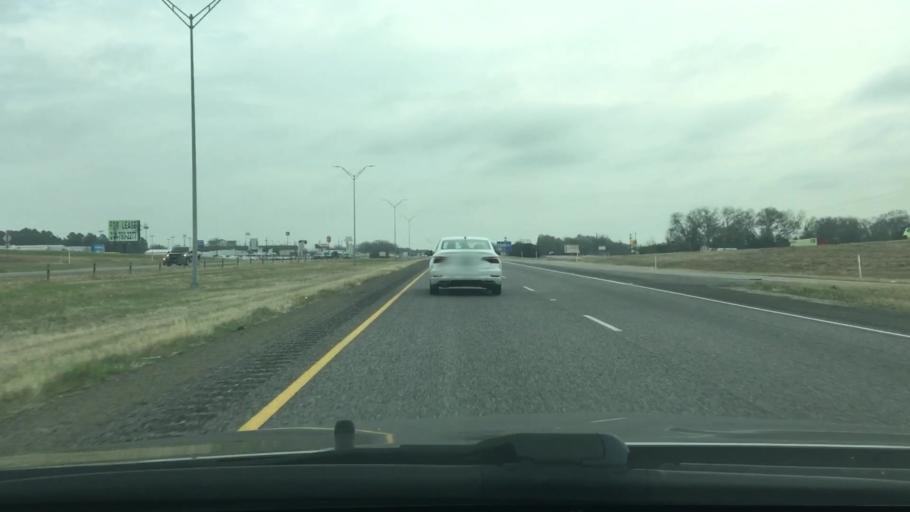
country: US
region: Texas
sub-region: Freestone County
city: Fairfield
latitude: 31.7254
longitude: -96.1801
